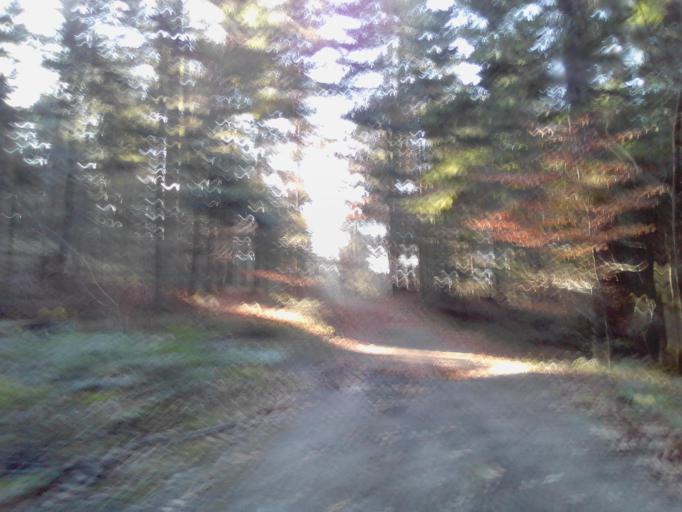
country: PL
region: Subcarpathian Voivodeship
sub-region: Powiat strzyzowski
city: Jawornik
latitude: 49.7921
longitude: 21.8856
